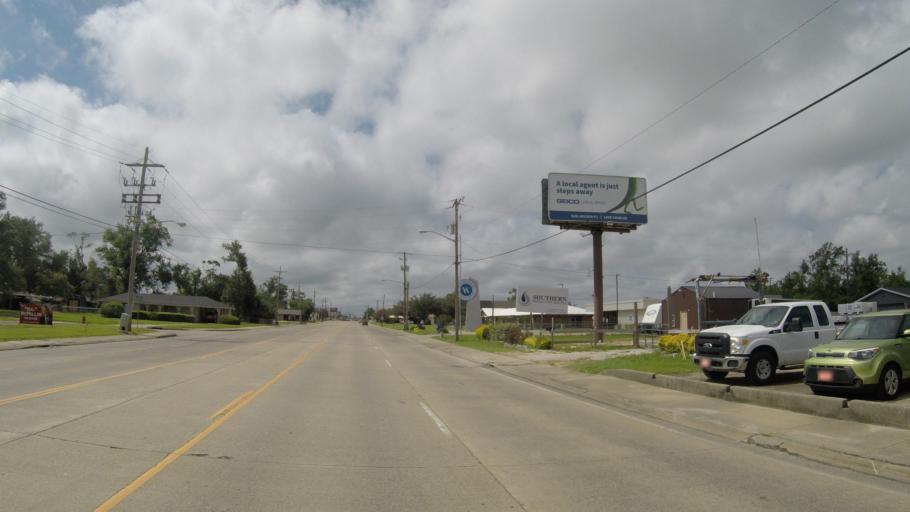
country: US
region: Louisiana
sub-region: Calcasieu Parish
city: Westlake
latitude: 30.2522
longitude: -93.2582
